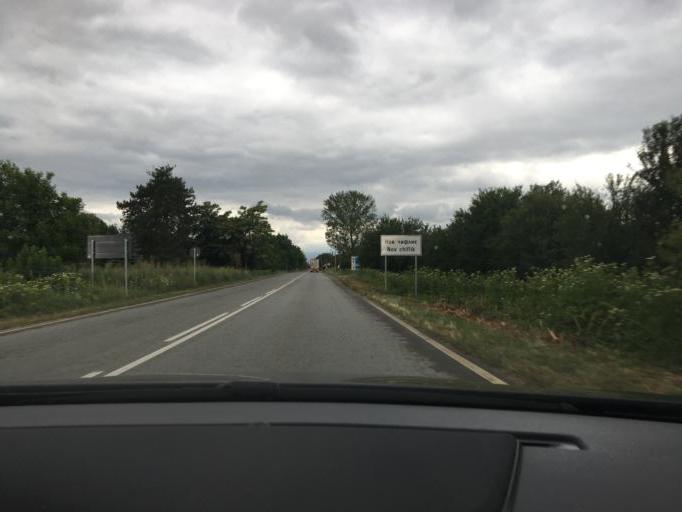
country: BG
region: Kyustendil
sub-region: Obshtina Kyustendil
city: Kyustendil
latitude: 42.2662
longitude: 22.8101
